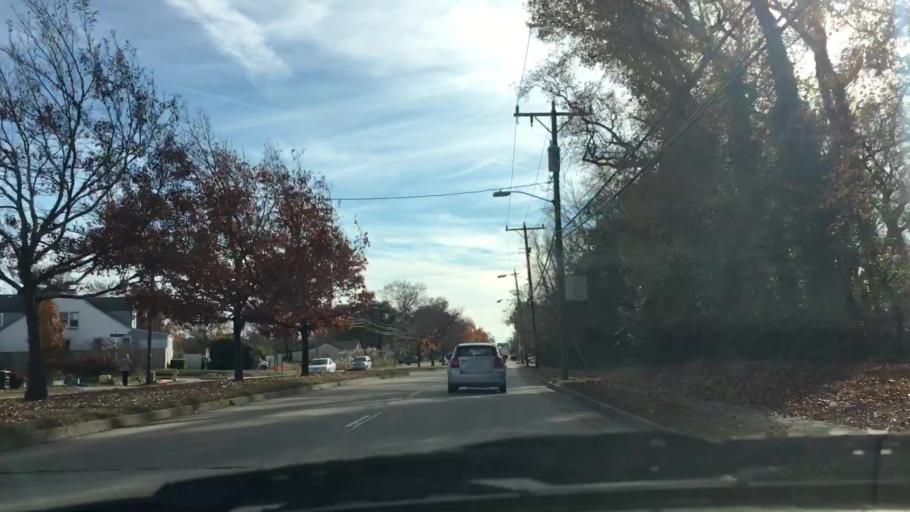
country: US
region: Virginia
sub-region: City of Norfolk
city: Norfolk
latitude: 36.9234
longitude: -76.2526
